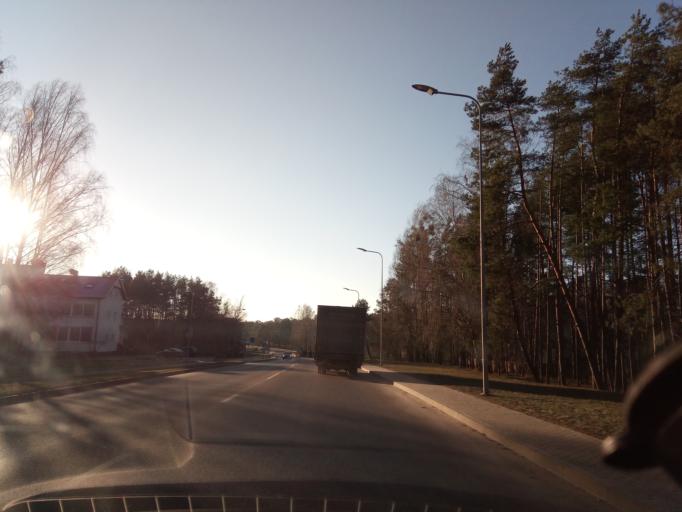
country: LT
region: Alytaus apskritis
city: Druskininkai
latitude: 54.0073
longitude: 23.9868
